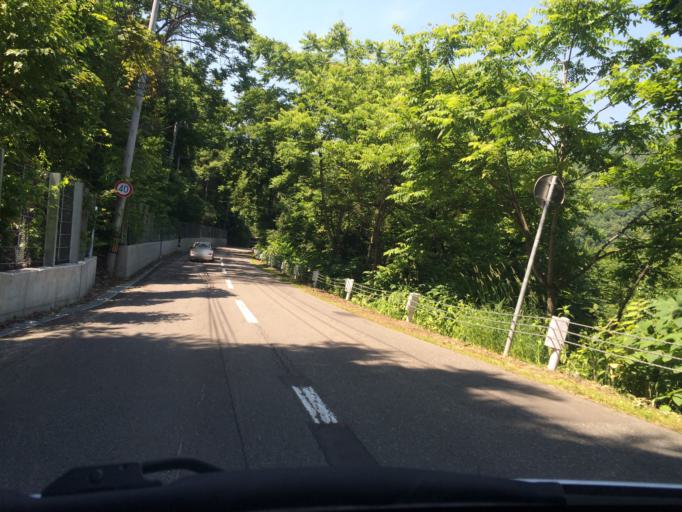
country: JP
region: Hokkaido
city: Sapporo
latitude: 42.9639
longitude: 141.2796
